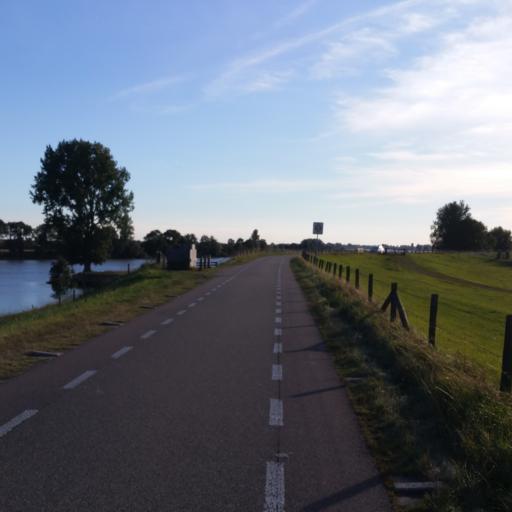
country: NL
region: Utrecht
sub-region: Gemeente Lopik
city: Lopik
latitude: 51.9792
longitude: 4.9962
